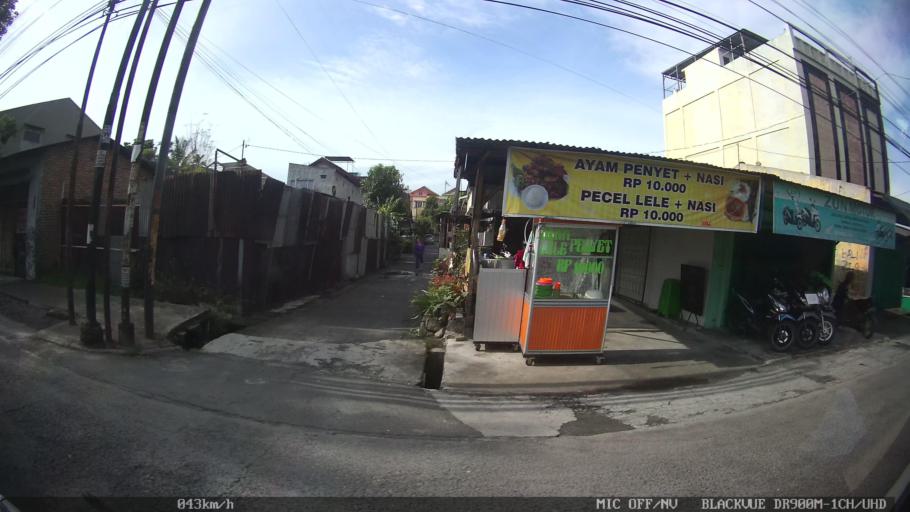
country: ID
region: North Sumatra
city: Sunggal
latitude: 3.6049
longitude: 98.6349
